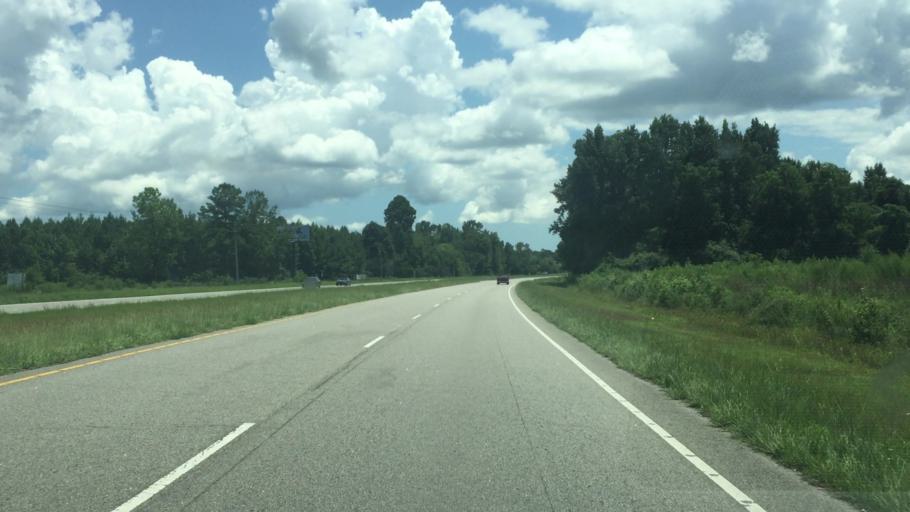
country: US
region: South Carolina
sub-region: Horry County
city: Loris
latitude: 33.9986
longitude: -78.7530
